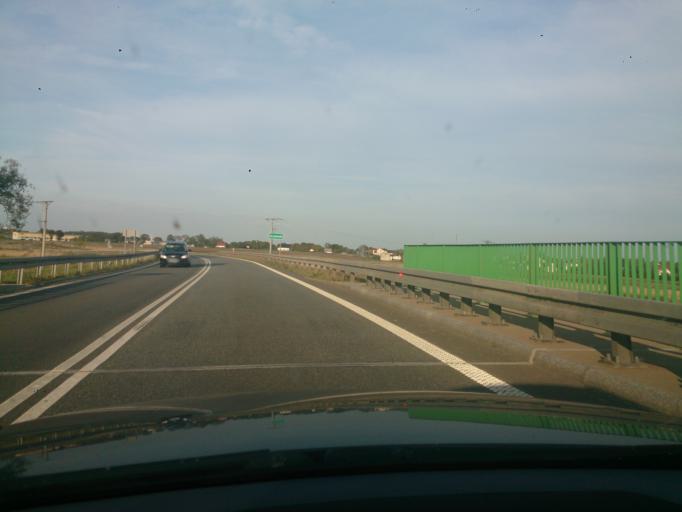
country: PL
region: Kujawsko-Pomorskie
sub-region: Grudziadz
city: Grudziadz
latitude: 53.4303
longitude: 18.7057
